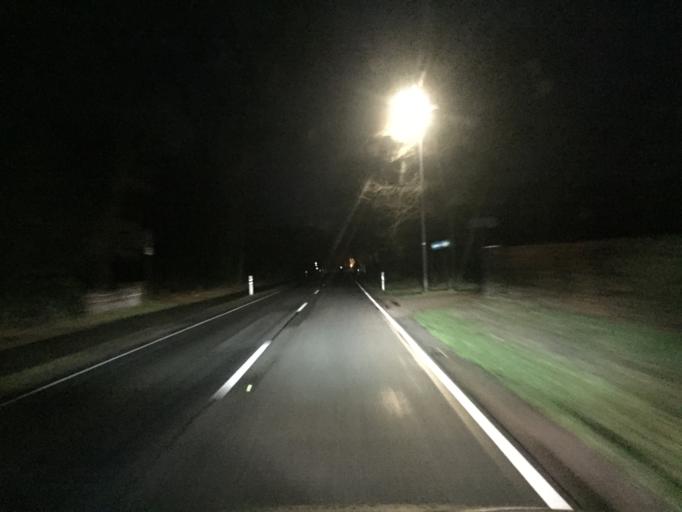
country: DE
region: Lower Saxony
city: Borstel
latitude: 52.6046
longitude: 8.9304
